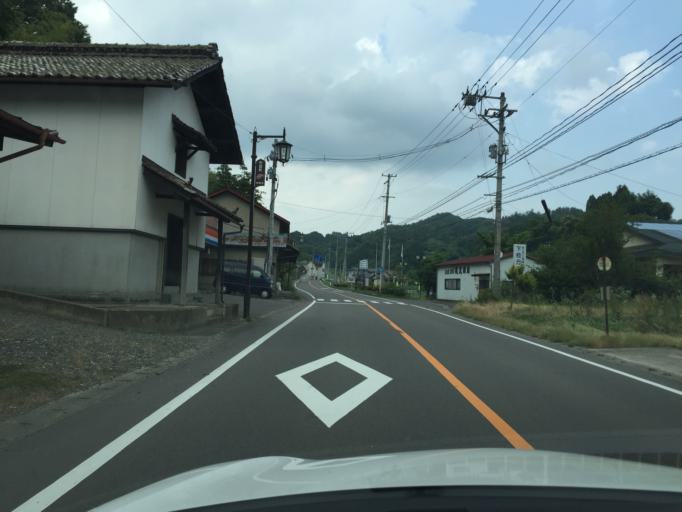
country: JP
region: Fukushima
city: Miharu
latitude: 37.3563
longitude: 140.4890
